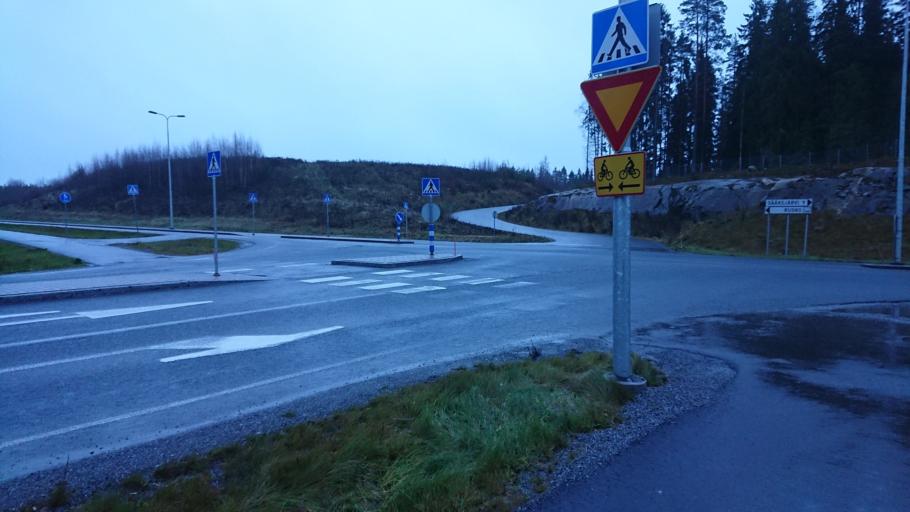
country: FI
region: Pirkanmaa
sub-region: Tampere
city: Tampere
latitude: 61.4417
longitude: 23.8762
